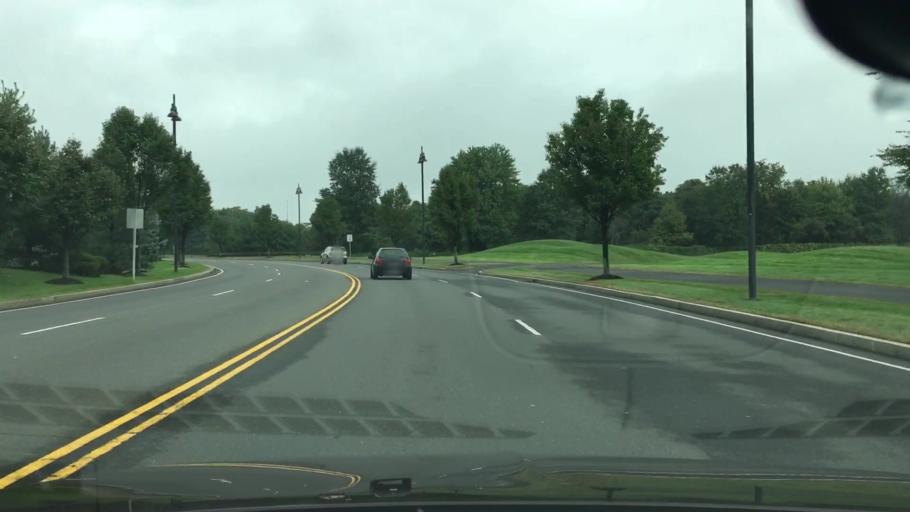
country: US
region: Connecticut
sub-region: Hartford County
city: East Hartford
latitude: 41.7595
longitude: -72.6229
